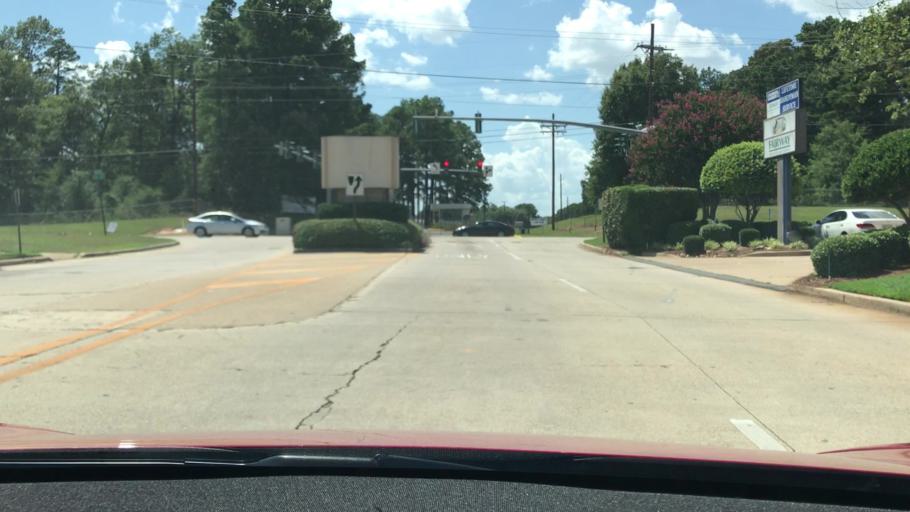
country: US
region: Louisiana
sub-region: Bossier Parish
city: Bossier City
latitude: 32.4183
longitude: -93.7360
